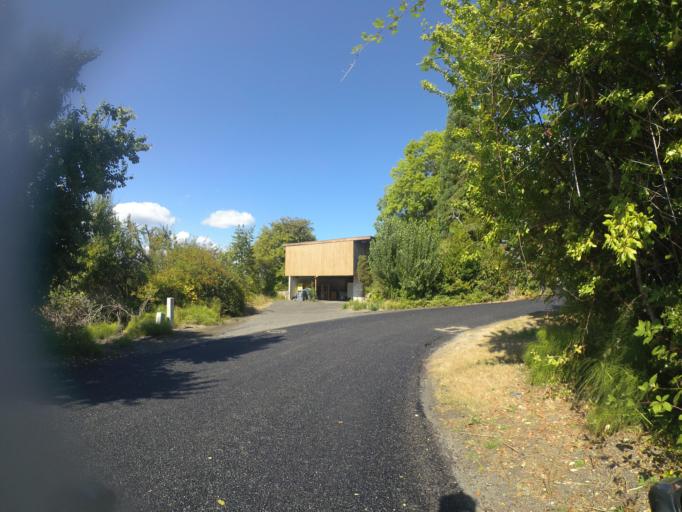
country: US
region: Washington
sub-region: Pierce County
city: University Place
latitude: 47.2347
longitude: -122.5620
